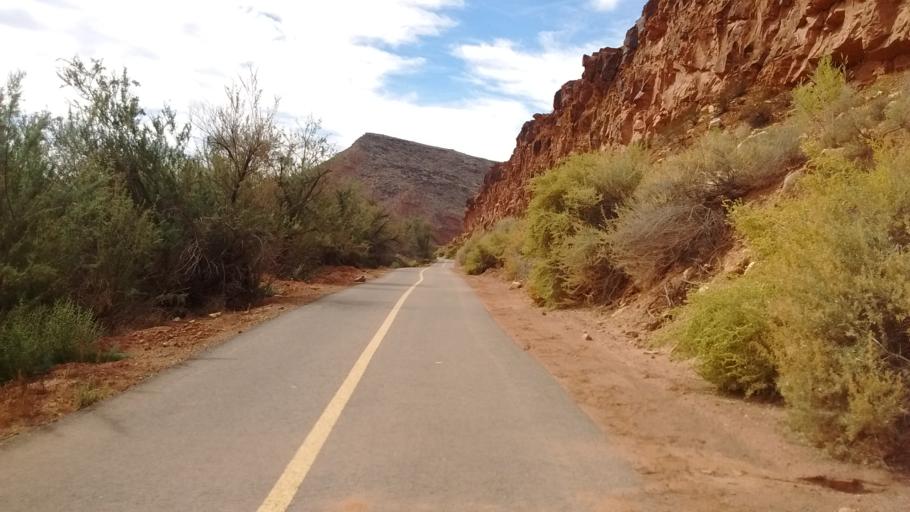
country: US
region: Utah
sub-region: Washington County
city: Washington
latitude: 37.1243
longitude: -113.4733
